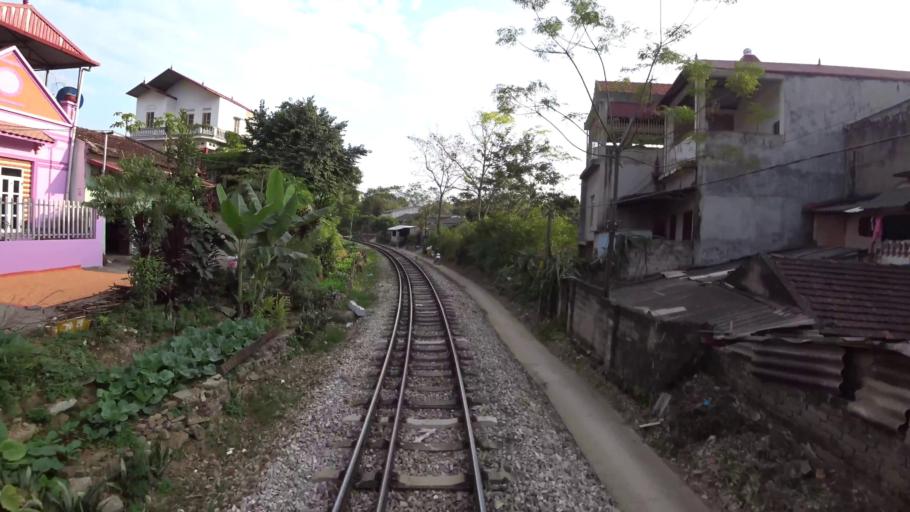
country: VN
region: Lang Son
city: Thi Tran Cao Loc
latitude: 21.9355
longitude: 106.6971
